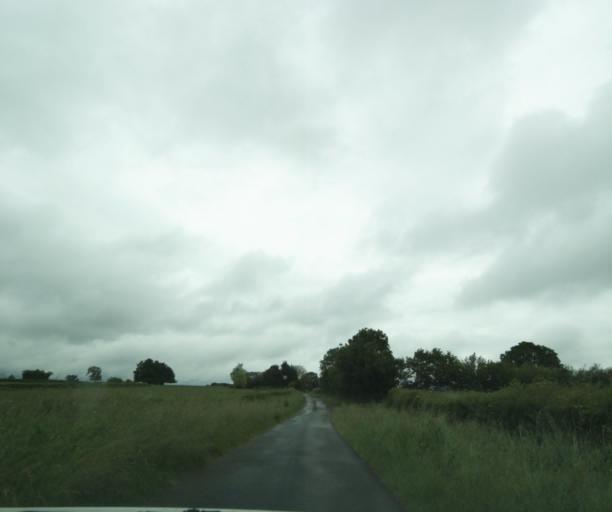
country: FR
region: Bourgogne
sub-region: Departement de Saone-et-Loire
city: Charolles
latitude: 46.5157
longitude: 4.2993
